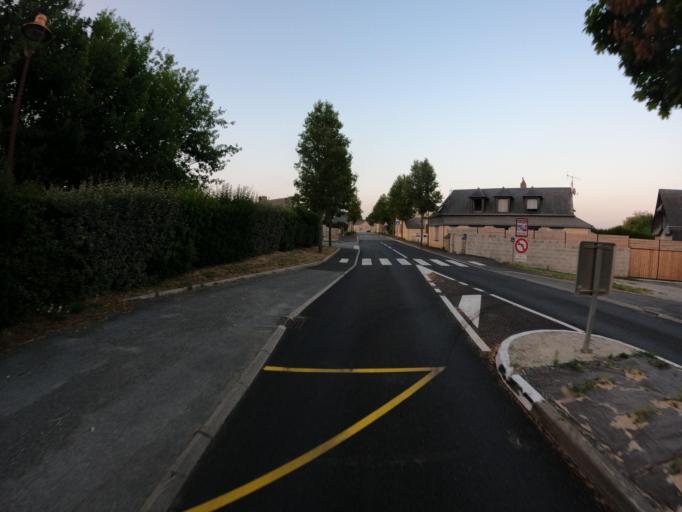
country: FR
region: Pays de la Loire
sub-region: Departement de la Mayenne
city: Chemaze
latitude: 47.7522
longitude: -0.7933
